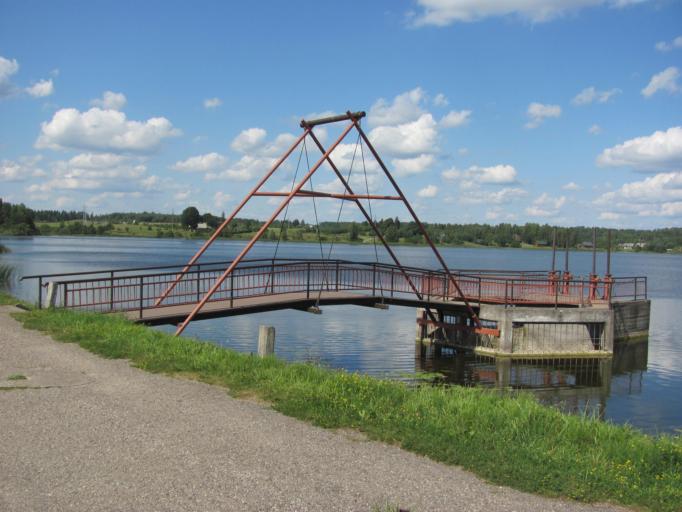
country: LT
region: Utenos apskritis
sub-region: Utena
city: Utena
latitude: 55.5164
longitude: 25.6338
